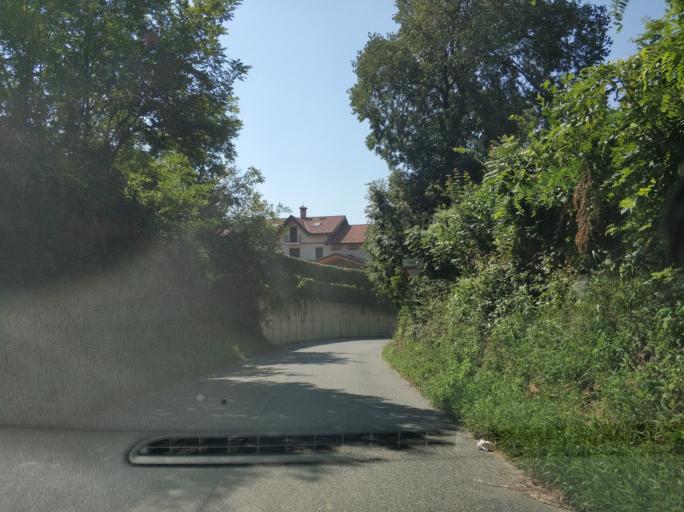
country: IT
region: Piedmont
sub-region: Provincia di Torino
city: San Francesco al Campo
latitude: 45.2308
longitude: 7.6395
